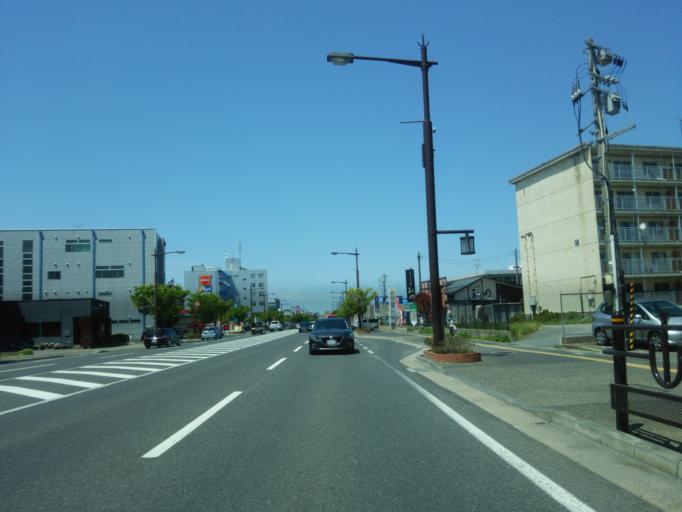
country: JP
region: Niigata
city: Kameda-honcho
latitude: 37.8900
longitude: 139.0704
